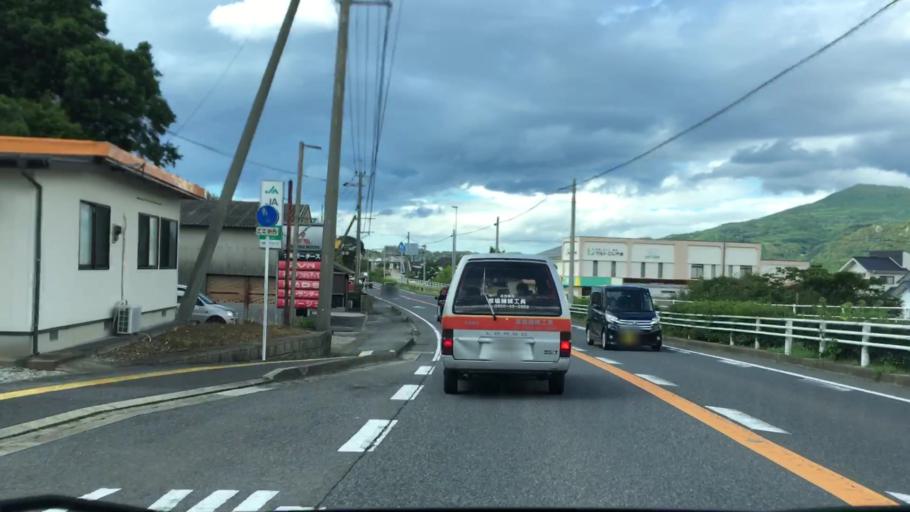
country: JP
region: Saga Prefecture
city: Imaricho-ko
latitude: 33.2062
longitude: 129.8505
